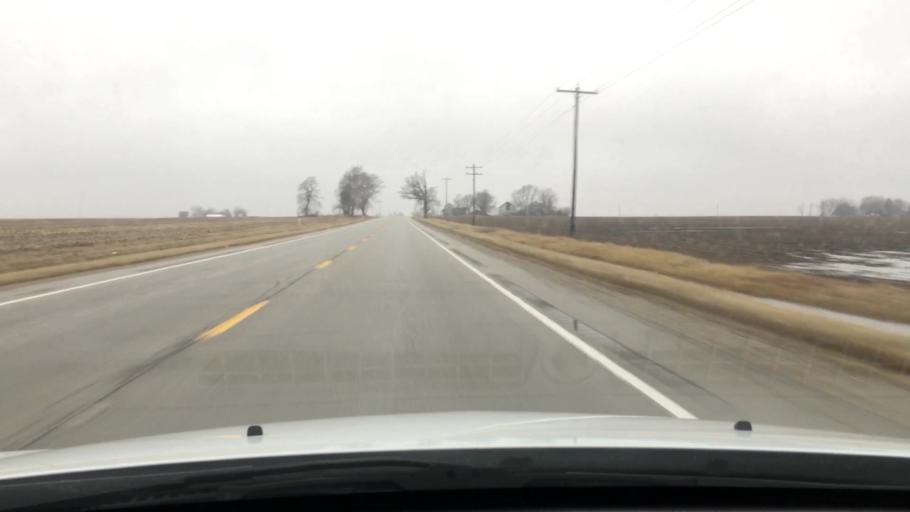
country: US
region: Illinois
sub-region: Livingston County
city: Flanagan
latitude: 40.8722
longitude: -88.7690
